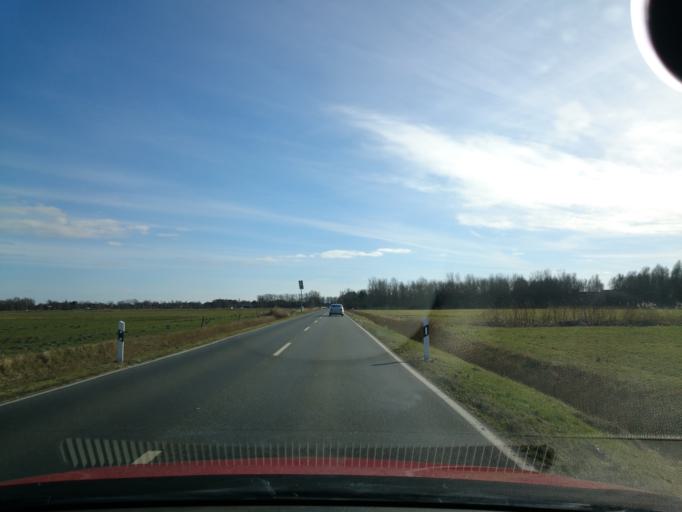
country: DE
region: Mecklenburg-Vorpommern
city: Ostseebad Dierhagen
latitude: 54.3019
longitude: 12.3526
